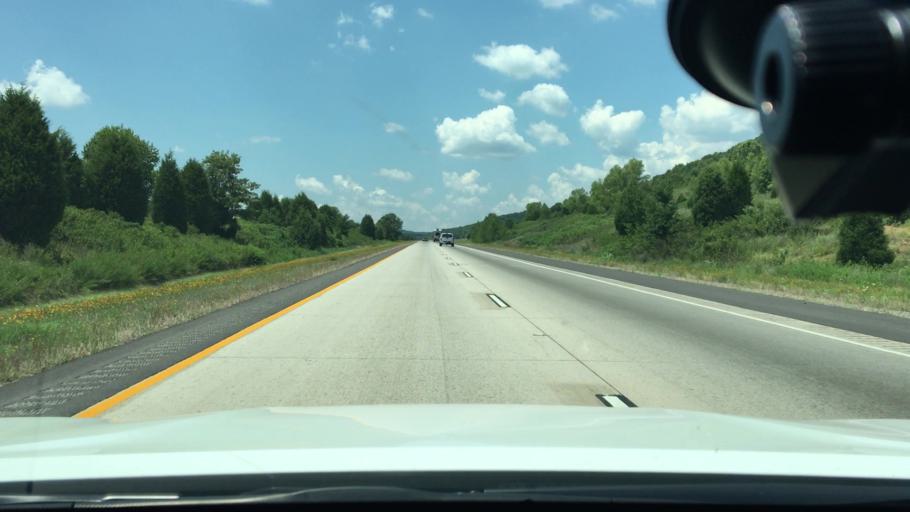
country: US
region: Arkansas
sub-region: Crawford County
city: Alma
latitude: 35.6869
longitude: -94.1758
